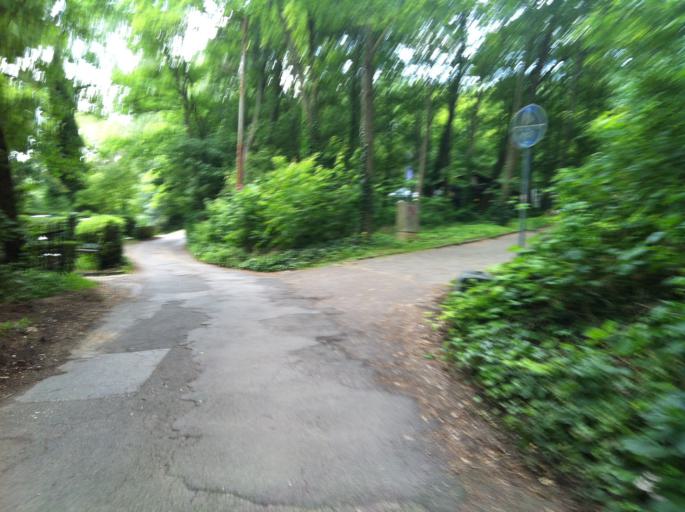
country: DE
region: Rheinland-Pfalz
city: Mainz
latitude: 50.0101
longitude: 8.2390
